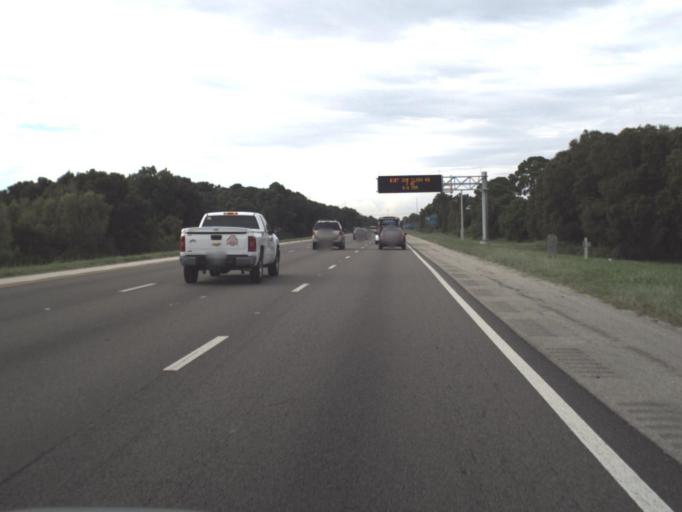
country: US
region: Florida
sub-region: Sarasota County
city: The Meadows
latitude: 27.3666
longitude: -82.4468
